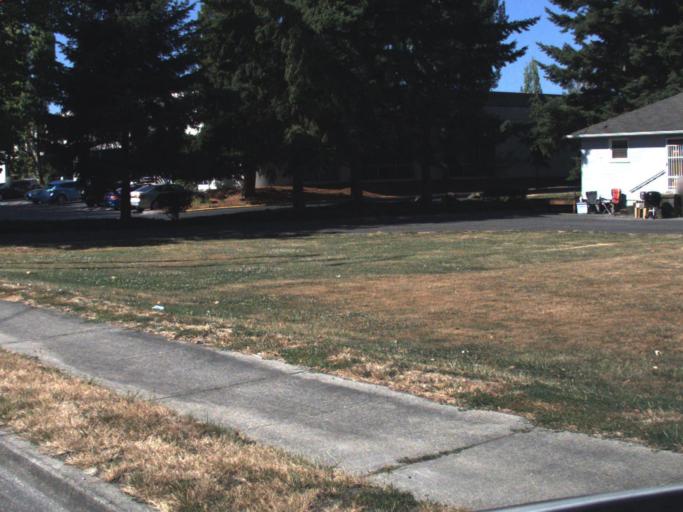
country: US
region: Washington
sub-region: King County
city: Kent
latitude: 47.4066
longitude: -122.2494
